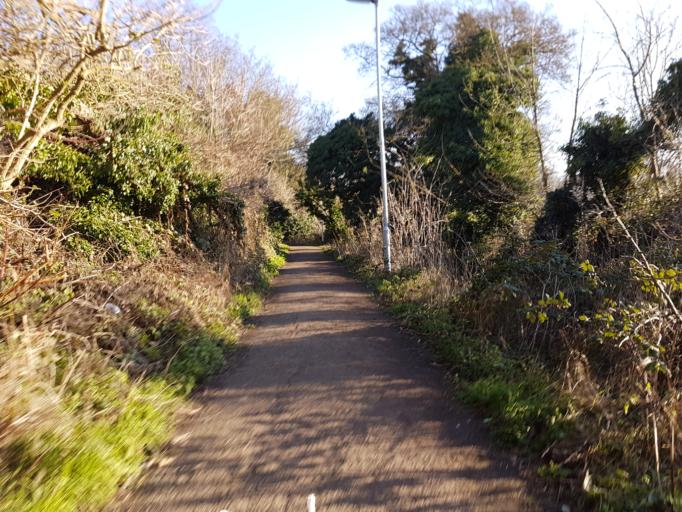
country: GB
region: England
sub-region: Cambridgeshire
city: Cambridge
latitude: 52.1878
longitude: 0.1657
